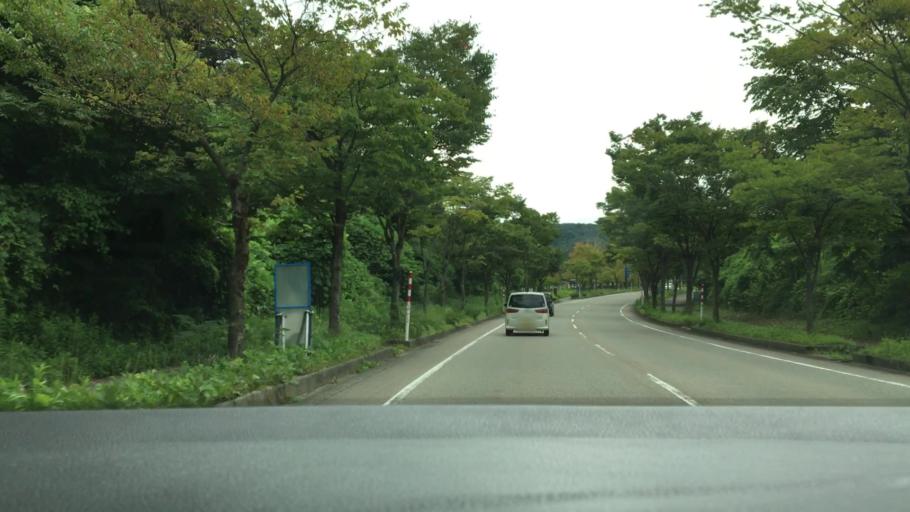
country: JP
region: Ishikawa
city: Nonoichi
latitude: 36.5508
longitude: 136.7052
